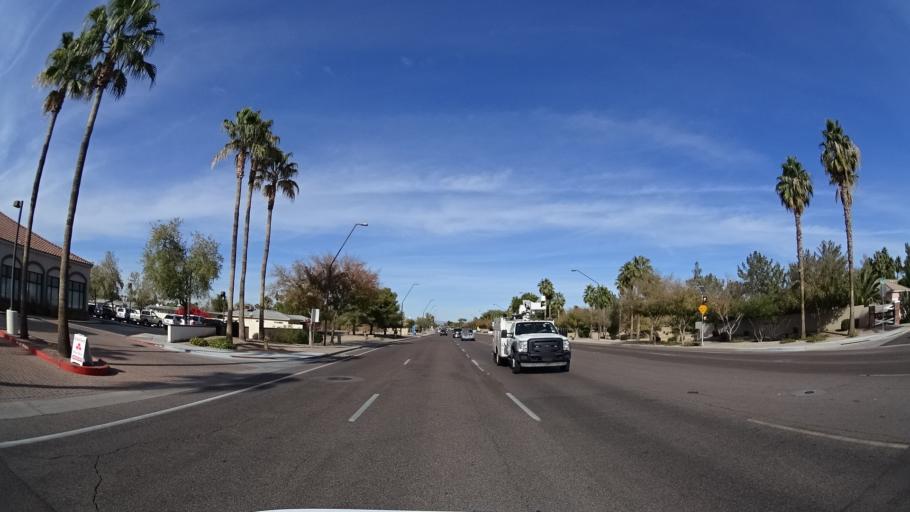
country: US
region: Arizona
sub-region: Maricopa County
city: Gilbert
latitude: 33.3417
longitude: -111.7898
